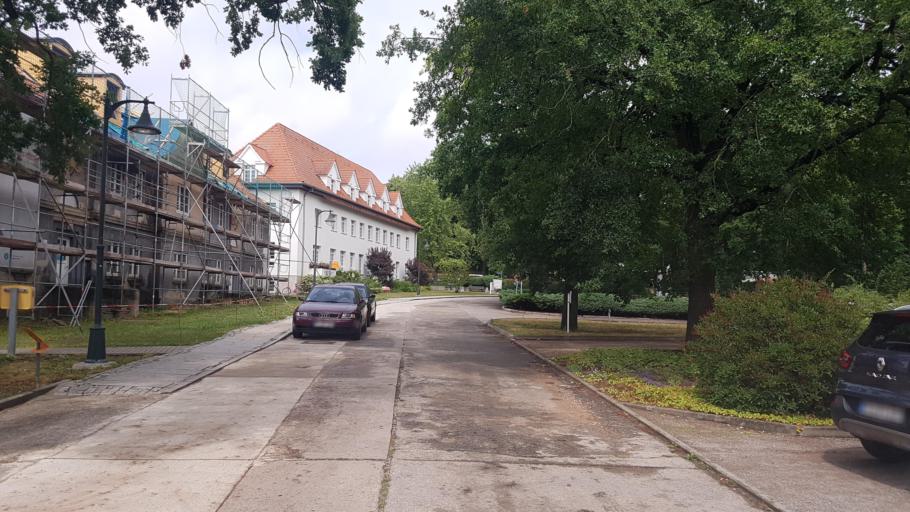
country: DE
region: Brandenburg
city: Trebbin
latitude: 52.2407
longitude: 13.1510
